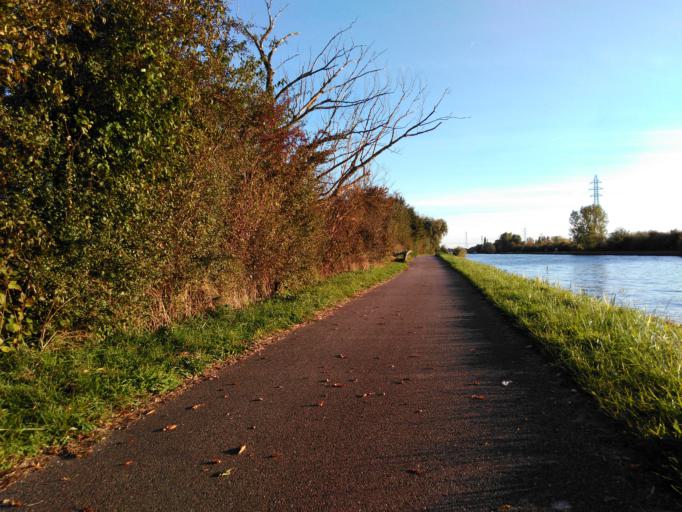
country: FR
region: Lorraine
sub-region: Departement de la Moselle
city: Maizieres-les-Metz
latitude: 49.2131
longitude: 6.1820
